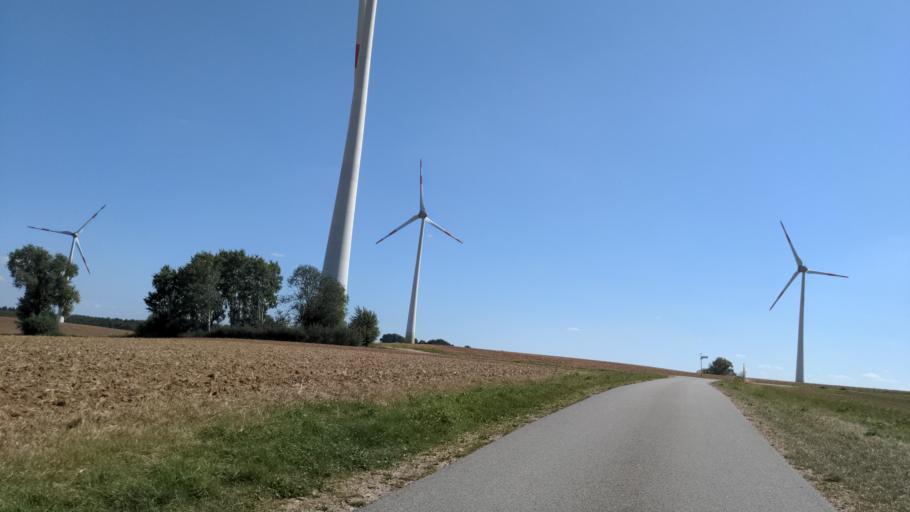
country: DE
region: Mecklenburg-Vorpommern
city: Selmsdorf
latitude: 53.8765
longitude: 10.8974
